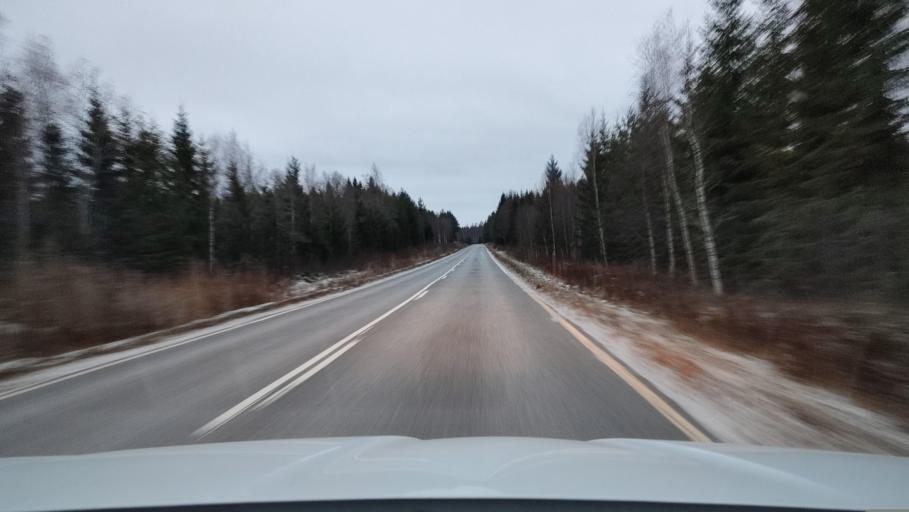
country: FI
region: Ostrobothnia
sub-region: Vaasa
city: Replot
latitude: 63.2433
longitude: 21.3821
